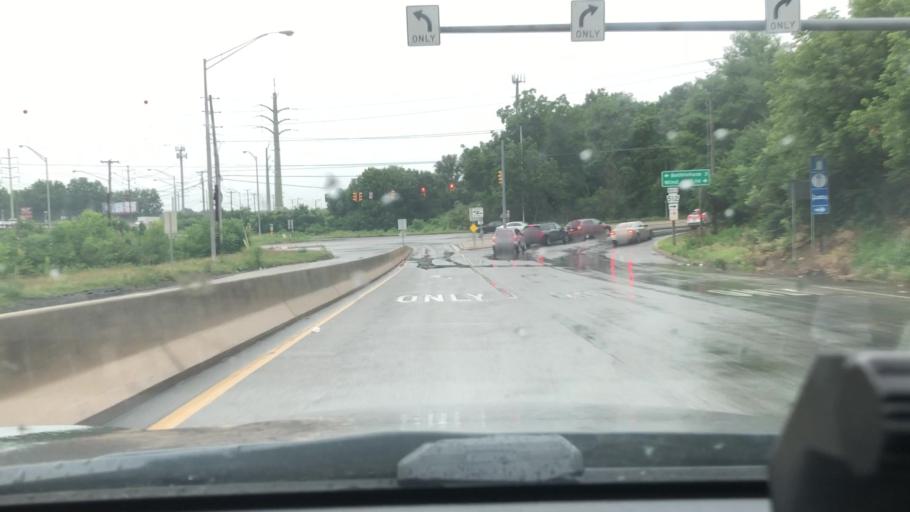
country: US
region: Pennsylvania
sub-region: Northampton County
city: Bethlehem
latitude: 40.6642
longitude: -75.3835
